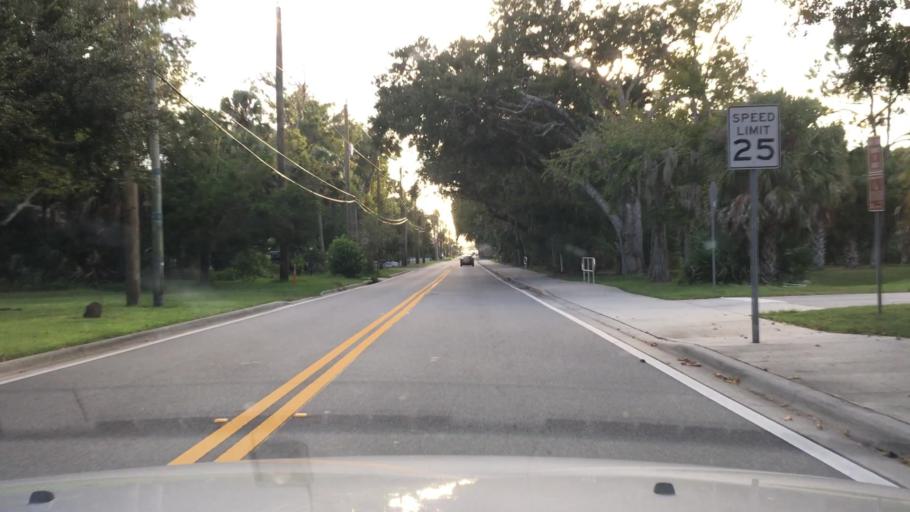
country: US
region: Florida
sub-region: Volusia County
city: Ormond Beach
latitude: 29.2662
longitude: -81.0697
